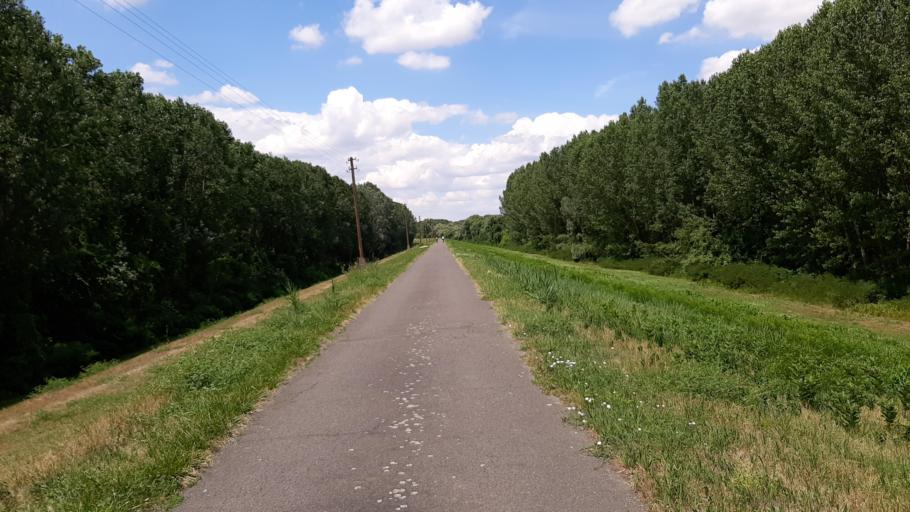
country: HU
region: Csongrad
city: Szentes
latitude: 46.6752
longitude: 20.2109
